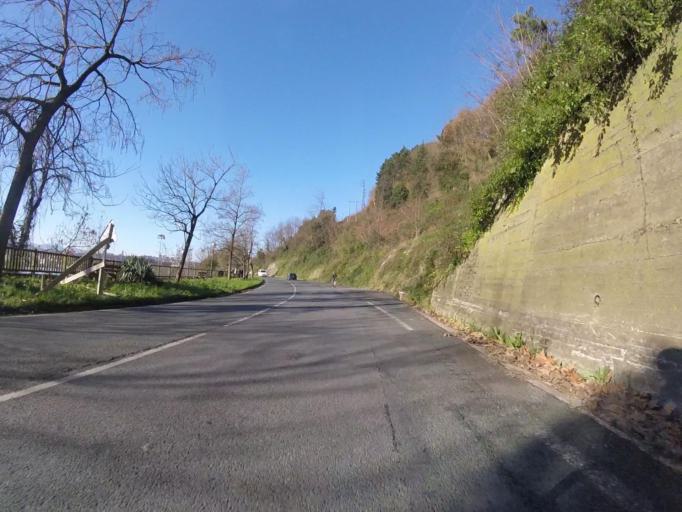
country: ES
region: Basque Country
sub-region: Provincia de Guipuzcoa
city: Lezo
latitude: 43.3246
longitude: -1.9036
